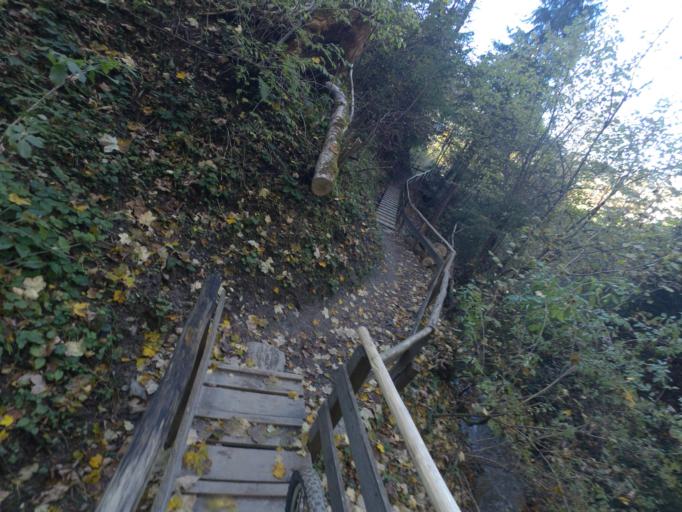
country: AT
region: Salzburg
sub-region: Politischer Bezirk Sankt Johann im Pongau
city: Sankt Johann im Pongau
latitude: 47.3503
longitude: 13.2100
